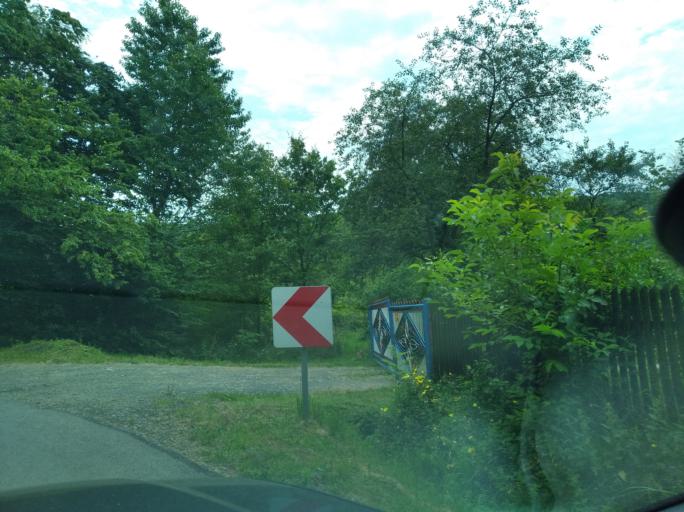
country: PL
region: Subcarpathian Voivodeship
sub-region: Powiat przeworski
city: Lopuszka Wielka
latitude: 49.9014
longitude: 22.4119
